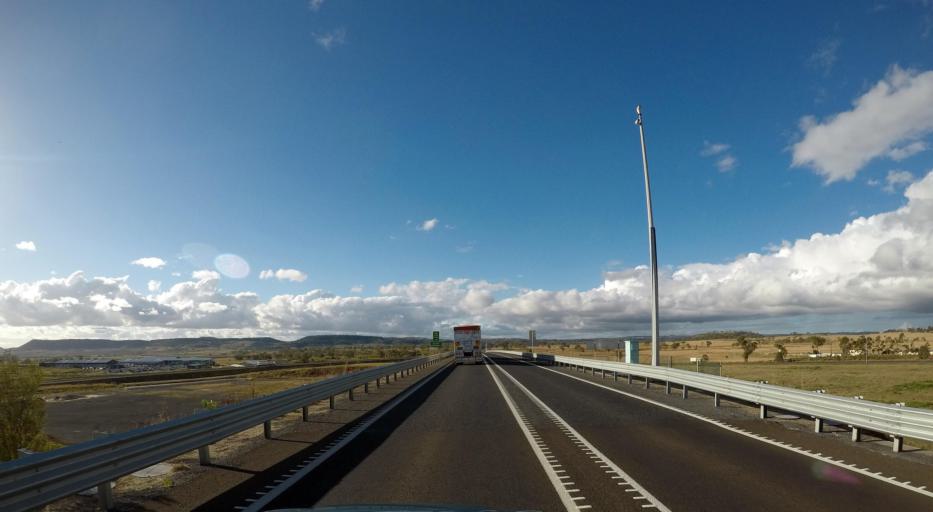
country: AU
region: Queensland
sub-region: Toowoomba
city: Wilsonton Heights
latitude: -27.5242
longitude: 151.8611
